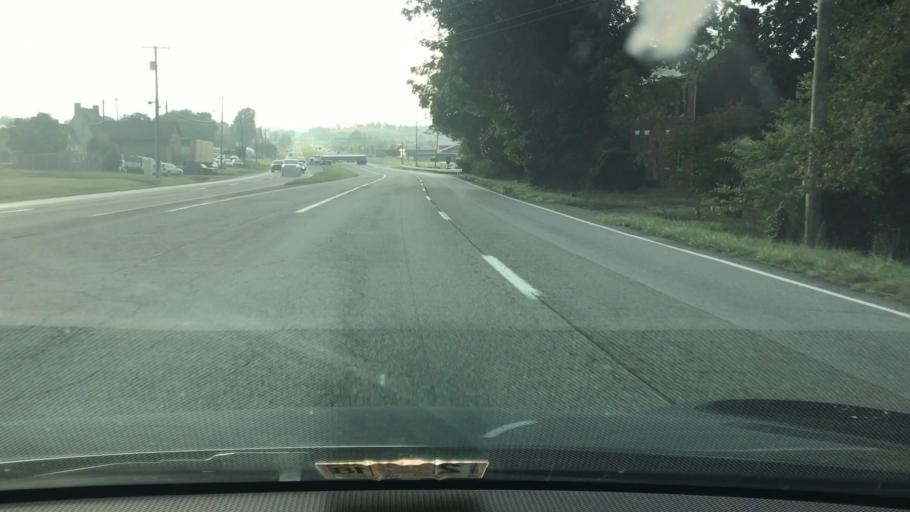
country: US
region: Virginia
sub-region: Botetourt County
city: Blue Ridge
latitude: 37.3868
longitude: -79.7375
